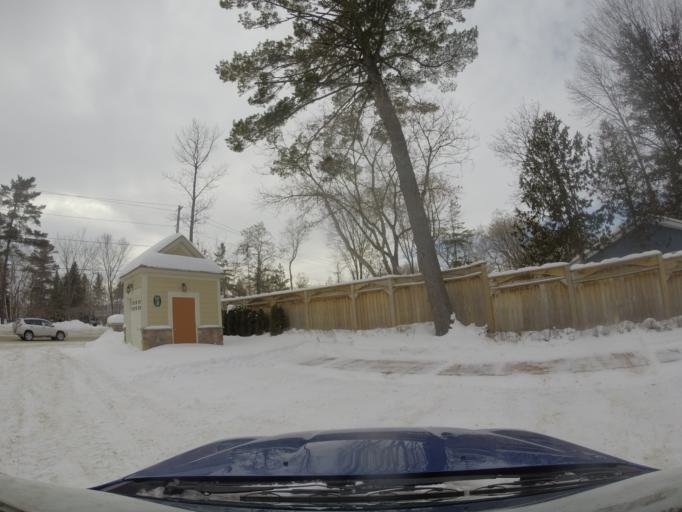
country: CA
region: Ontario
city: Wasaga Beach
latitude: 44.5311
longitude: -80.0093
